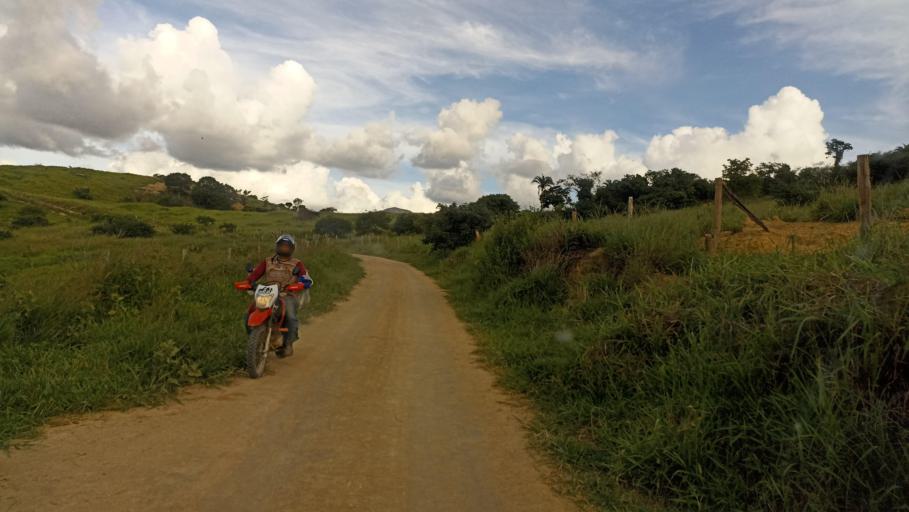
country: BR
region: Minas Gerais
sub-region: Almenara
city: Almenara
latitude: -16.5485
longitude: -40.4527
